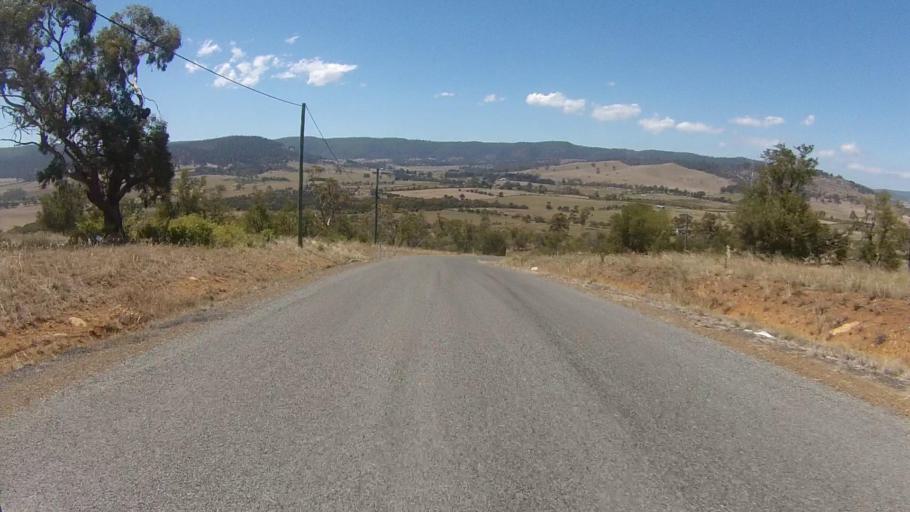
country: AU
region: Tasmania
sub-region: Sorell
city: Sorell
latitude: -42.7581
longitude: 147.5577
